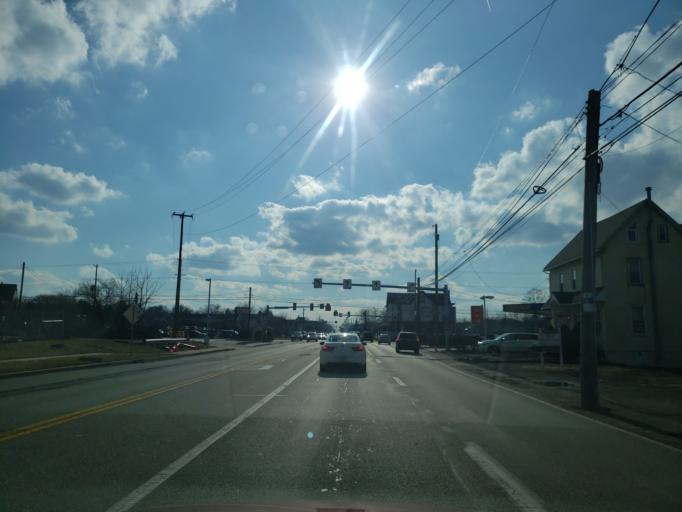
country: US
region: Pennsylvania
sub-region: Montgomery County
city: Blue Bell
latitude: 40.1678
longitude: -75.2895
